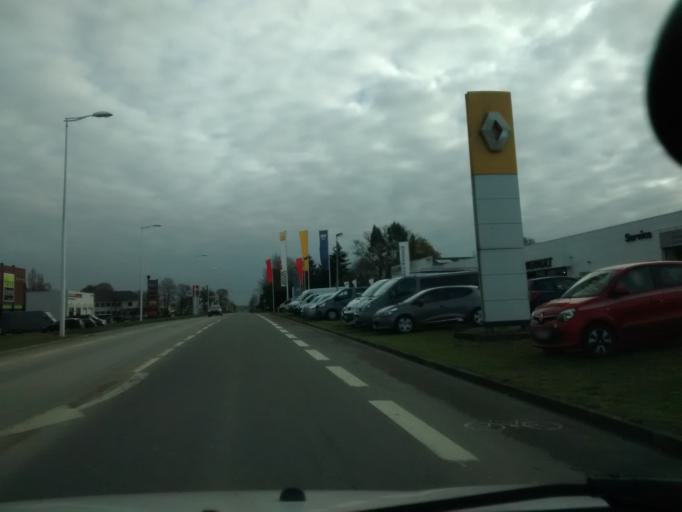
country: FR
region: Brittany
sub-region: Departement d'Ille-et-Vilaine
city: Vitre
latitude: 48.1210
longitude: -1.1784
